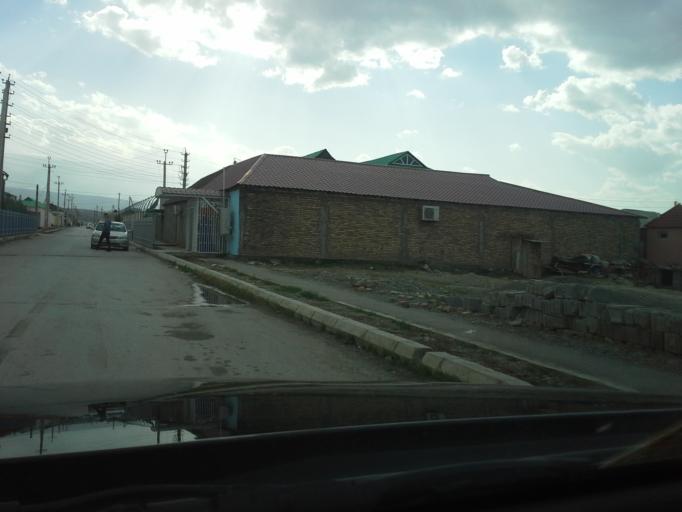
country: TM
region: Ahal
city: Ashgabat
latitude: 37.9941
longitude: 58.2967
